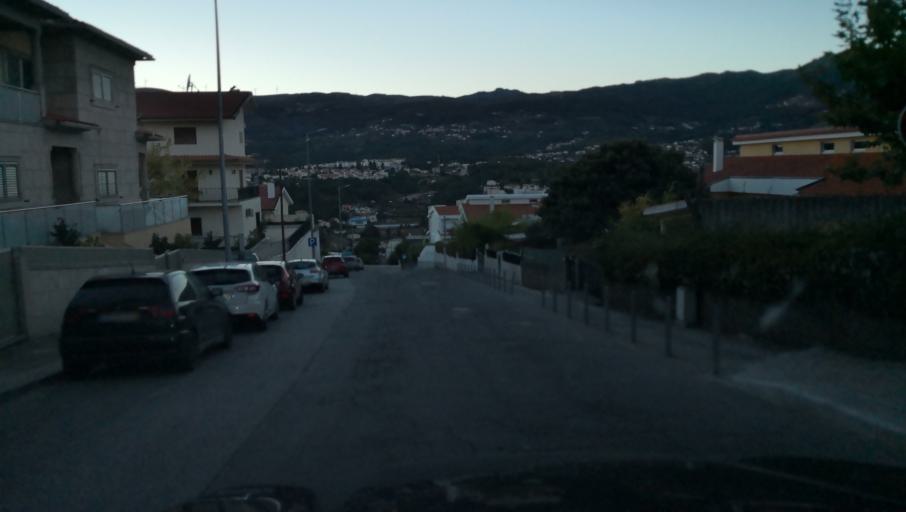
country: PT
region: Vila Real
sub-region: Vila Real
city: Vila Real
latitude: 41.3012
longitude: -7.7508
